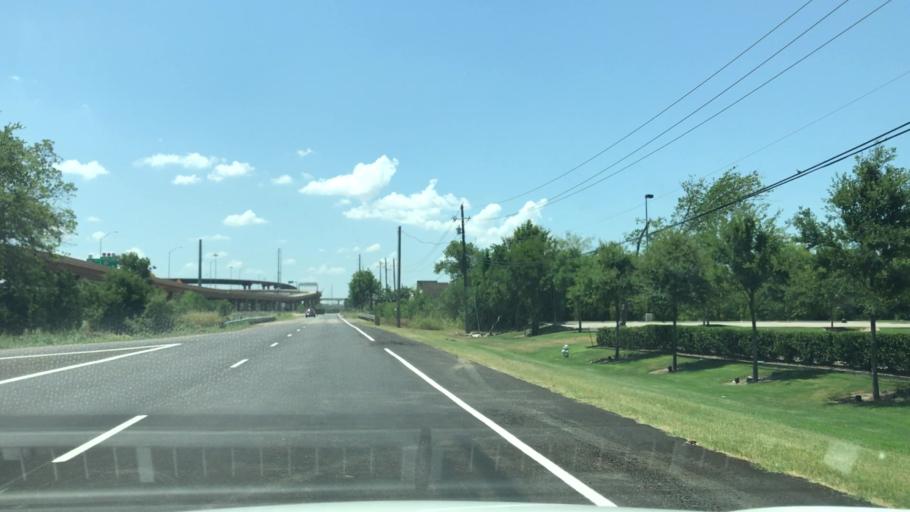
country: US
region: Texas
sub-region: Dallas County
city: Farmers Branch
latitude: 32.9168
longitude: -96.9002
